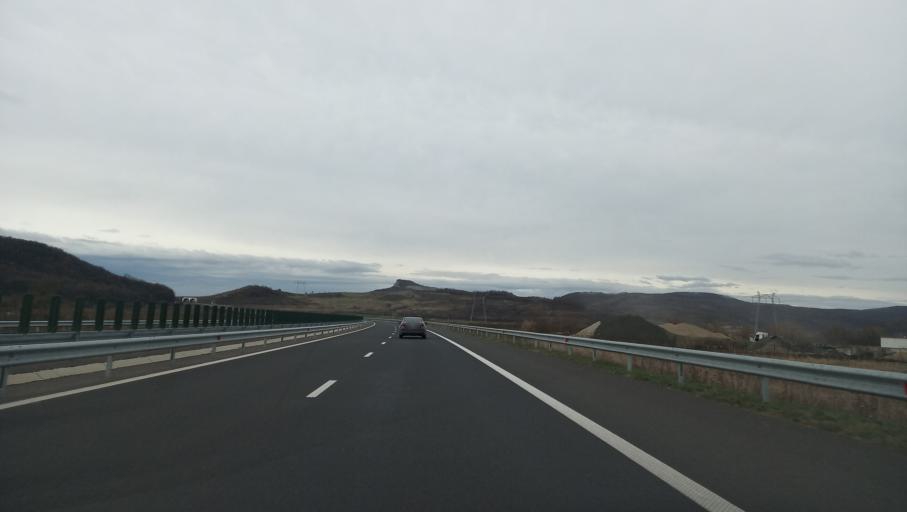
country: RO
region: Hunedoara
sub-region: Comuna Branisca
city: Branisca
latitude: 45.9331
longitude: 22.7603
